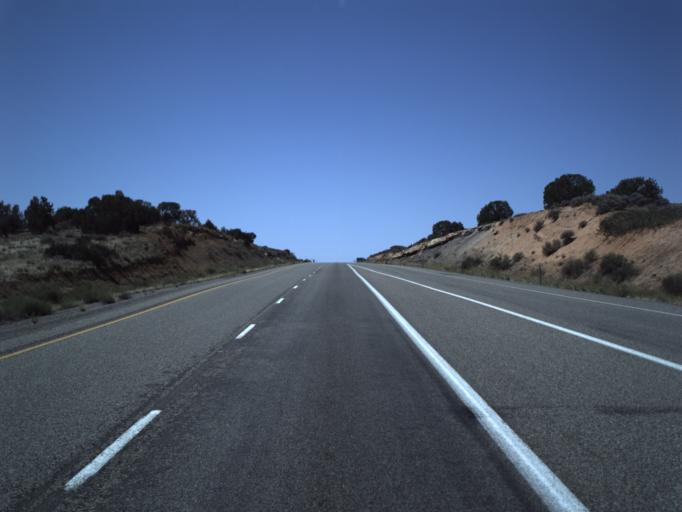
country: US
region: Colorado
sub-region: Mesa County
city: Loma
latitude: 39.1831
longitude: -109.1197
